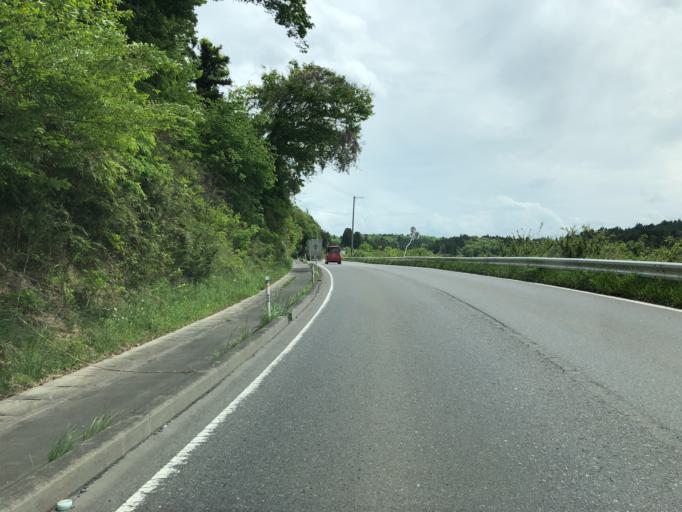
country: JP
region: Fukushima
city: Ishikawa
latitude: 37.0920
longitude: 140.3529
